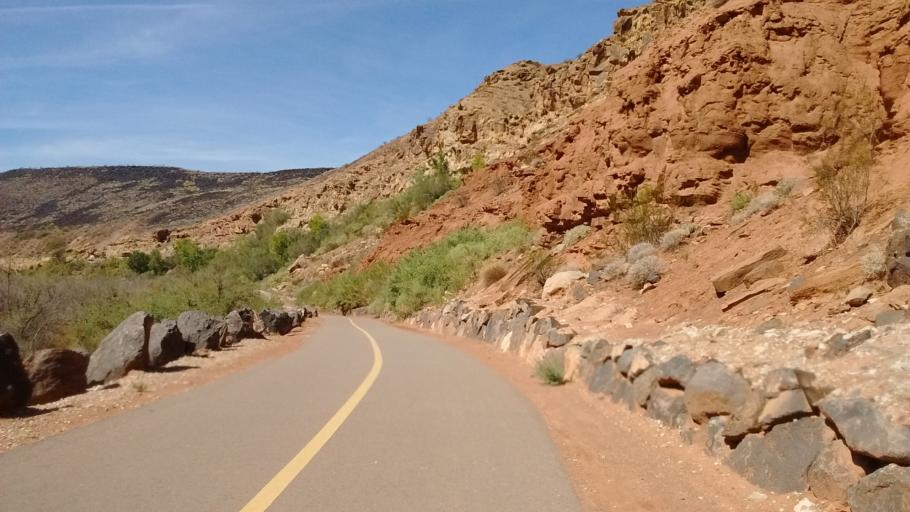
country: US
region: Utah
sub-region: Washington County
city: Washington
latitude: 37.1244
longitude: -113.4896
